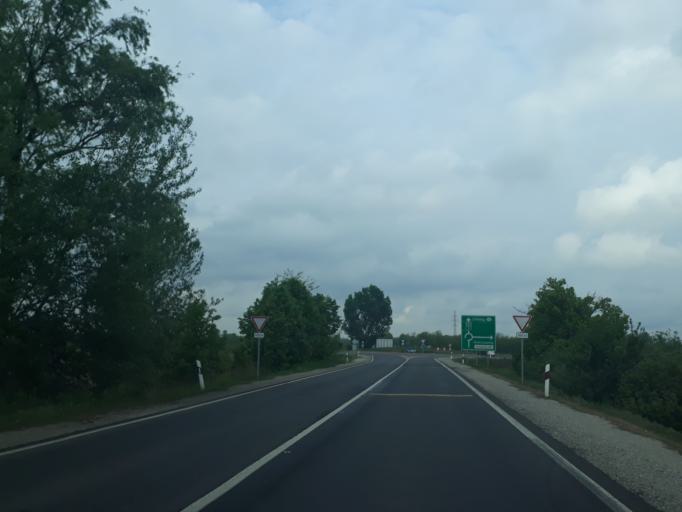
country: HU
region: Szabolcs-Szatmar-Bereg
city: Ajak
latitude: 48.2060
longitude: 22.0513
